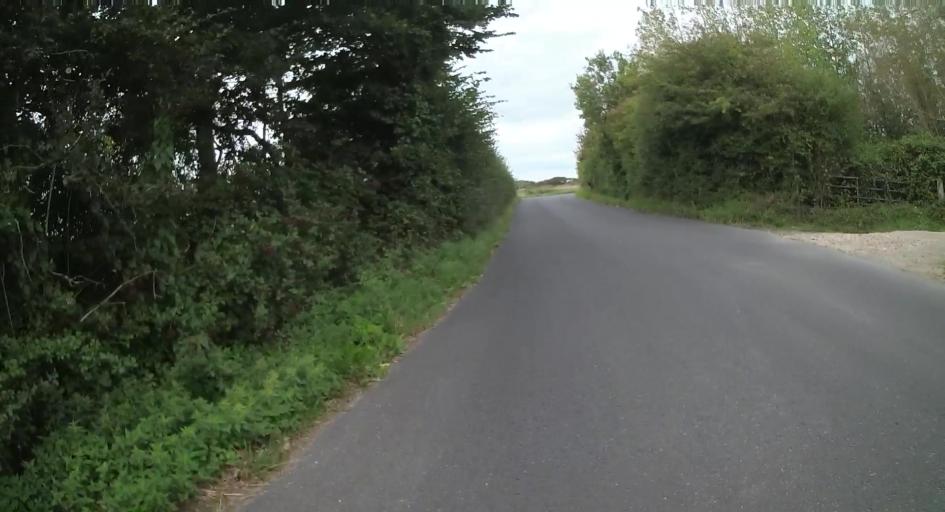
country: GB
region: England
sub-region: Isle of Wight
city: Freshwater
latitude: 50.6782
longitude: -1.4963
